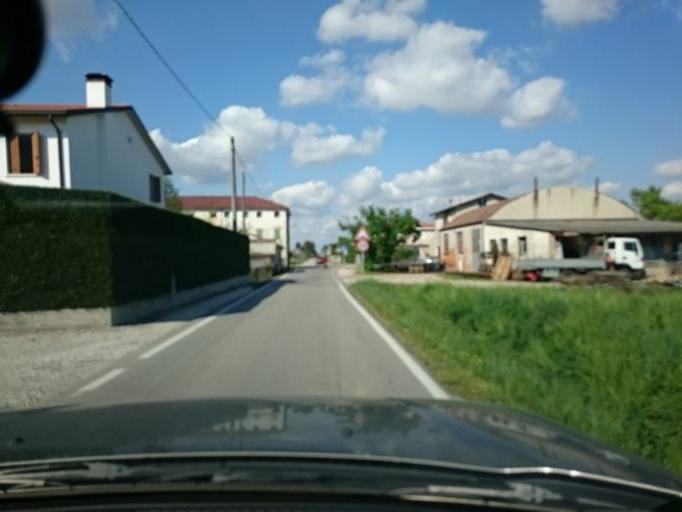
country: IT
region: Veneto
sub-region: Provincia di Padova
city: Villanova
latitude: 45.4866
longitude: 11.9857
